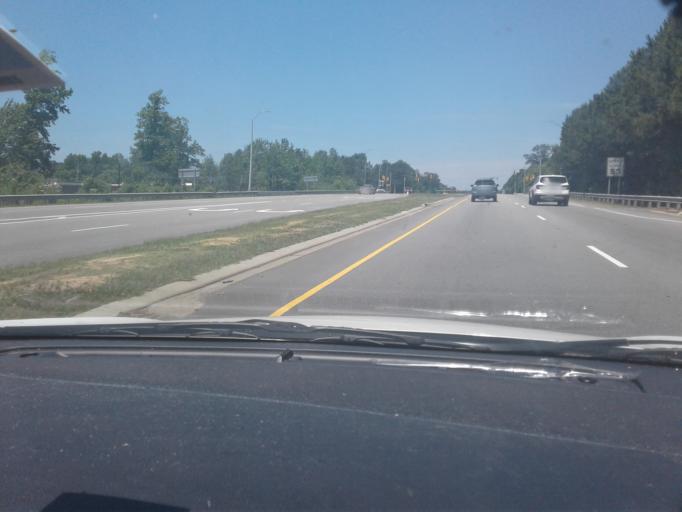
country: US
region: North Carolina
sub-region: Wake County
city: Holly Springs
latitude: 35.6414
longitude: -78.8370
